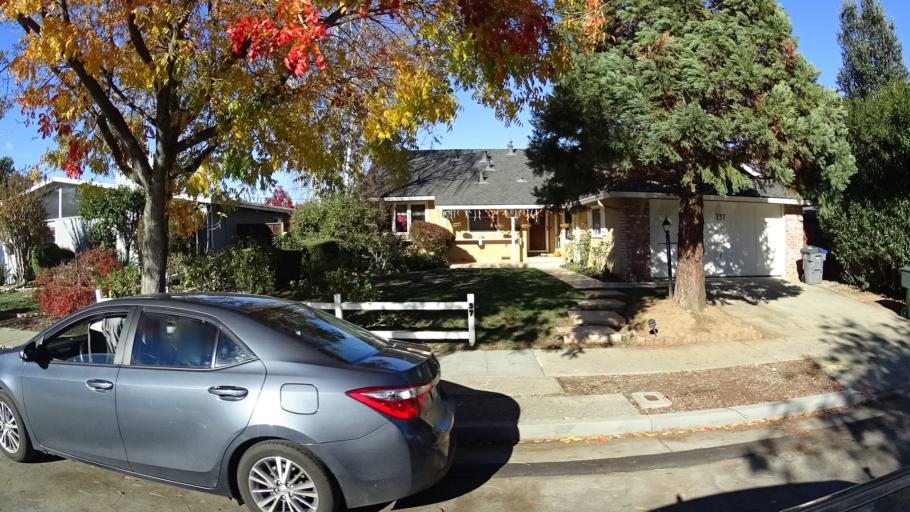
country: US
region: California
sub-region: Santa Clara County
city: Sunnyvale
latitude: 37.3485
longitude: -122.0214
